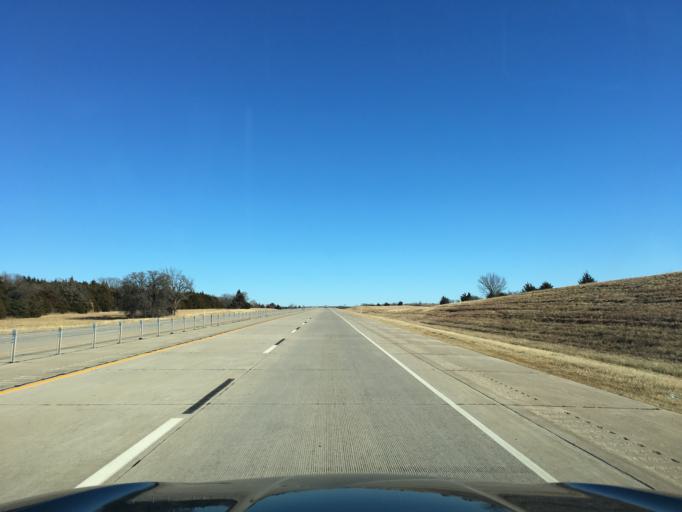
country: US
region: Oklahoma
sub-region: Payne County
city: Yale
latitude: 36.2250
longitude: -96.6734
